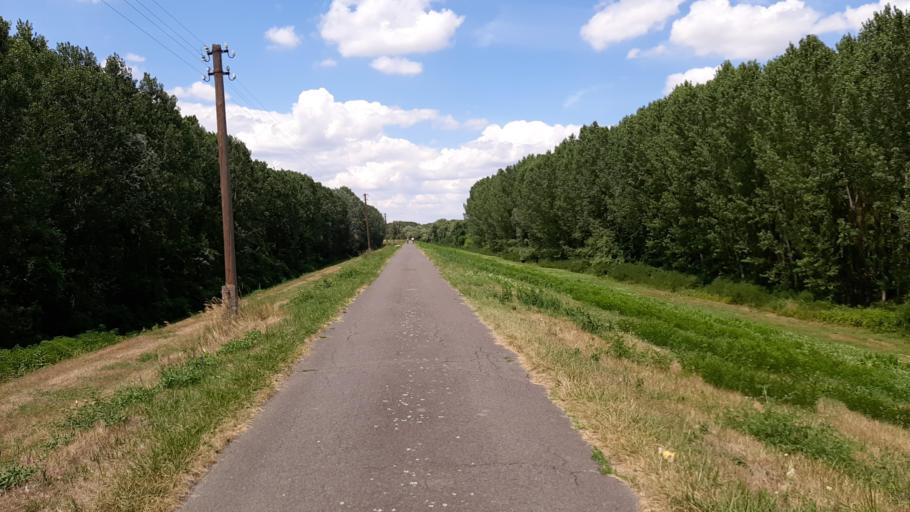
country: HU
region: Csongrad
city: Szentes
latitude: 46.6750
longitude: 20.2112
